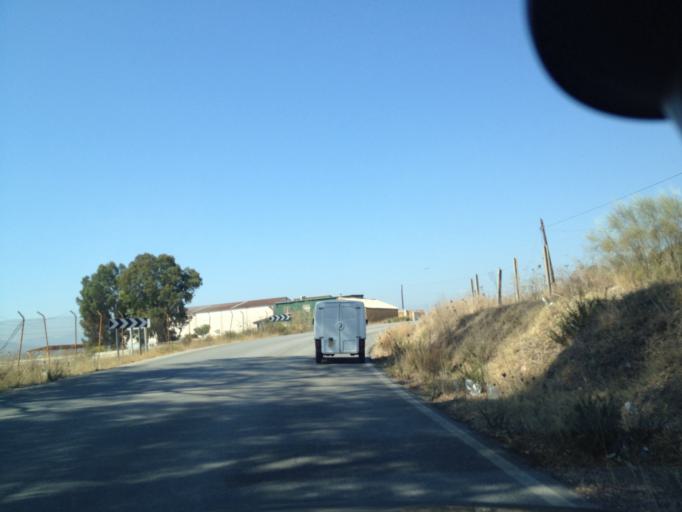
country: ES
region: Andalusia
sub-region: Provincia de Malaga
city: Alhaurin de la Torre
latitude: 36.7188
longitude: -4.5223
